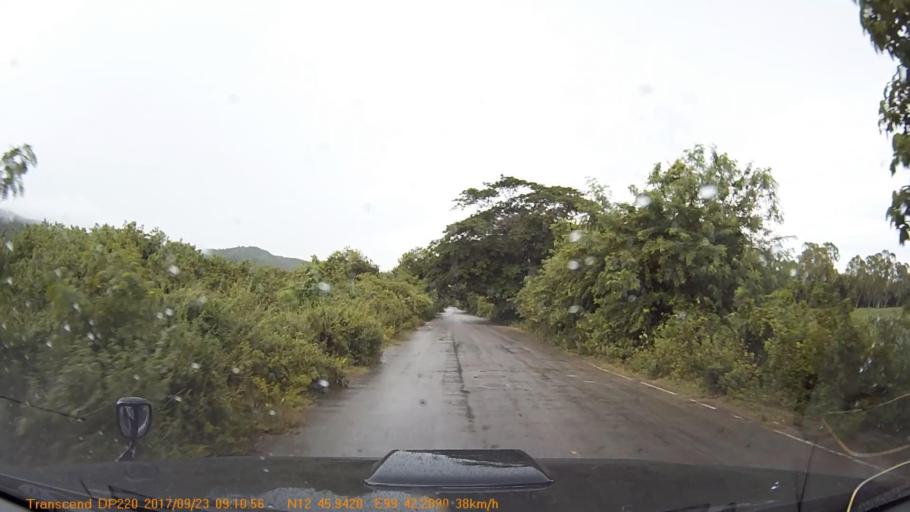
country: TH
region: Phetchaburi
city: Kaeng Krachan
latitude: 12.7657
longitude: 99.7035
